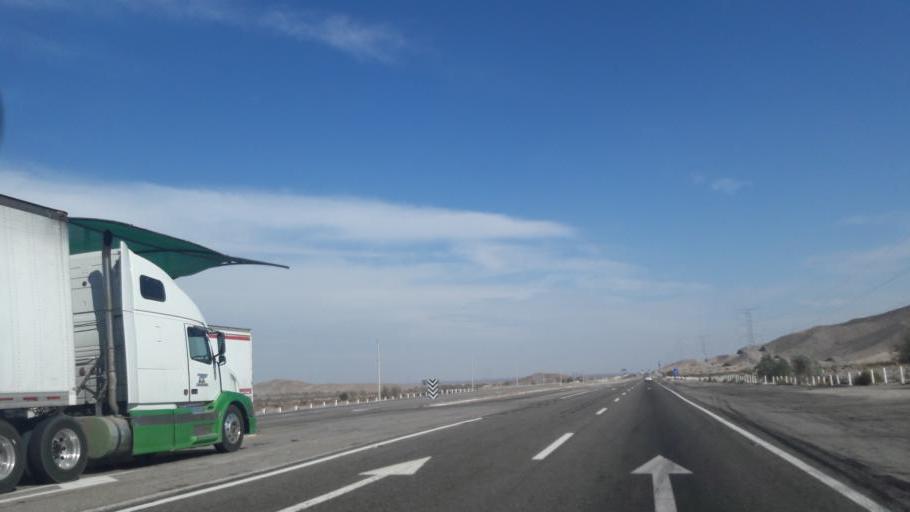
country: MX
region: Baja California
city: Progreso
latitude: 32.5836
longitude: -115.7132
